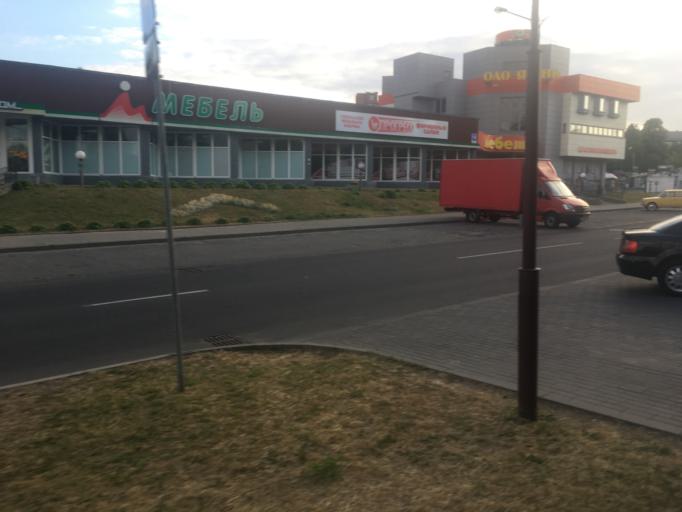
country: BY
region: Grodnenskaya
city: Hrodna
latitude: 53.6936
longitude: 23.8272
